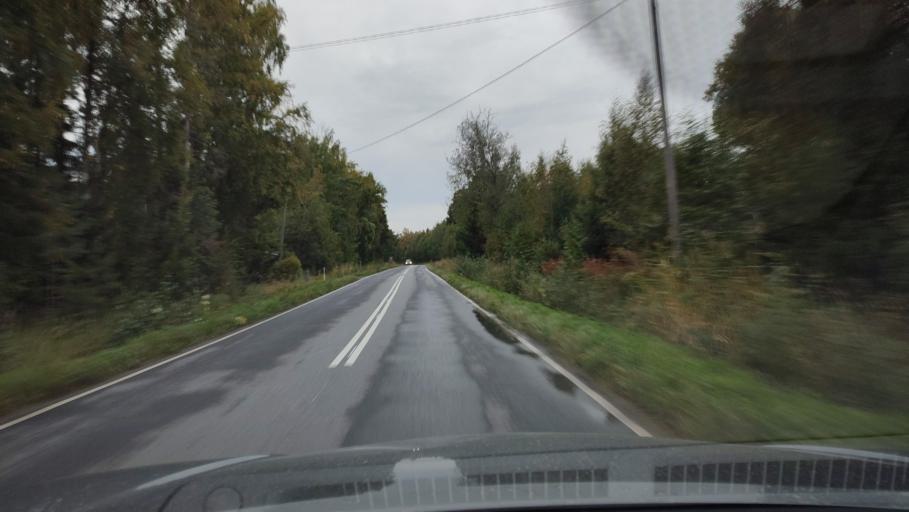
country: FI
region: Ostrobothnia
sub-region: Sydosterbotten
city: Kristinestad
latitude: 62.3124
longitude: 21.3595
